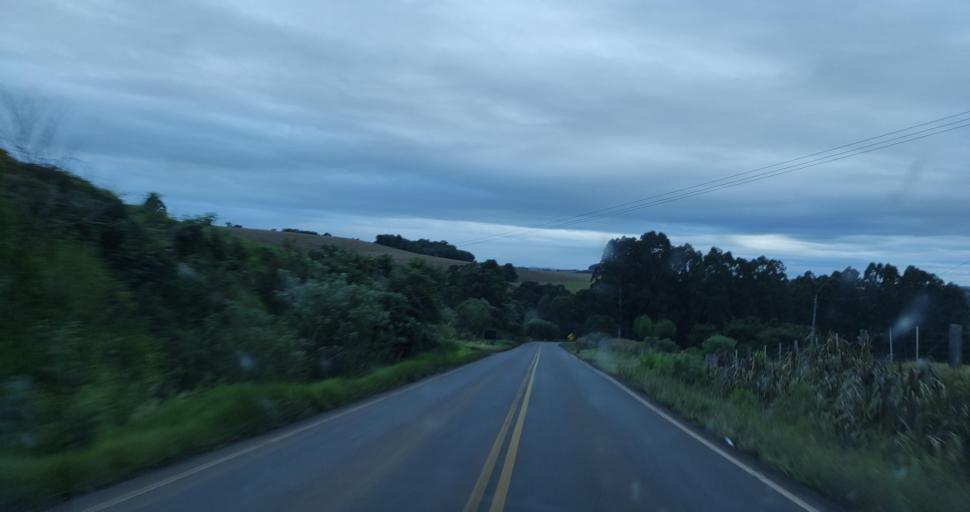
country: BR
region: Santa Catarina
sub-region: Xanxere
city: Xanxere
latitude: -26.7289
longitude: -52.4010
